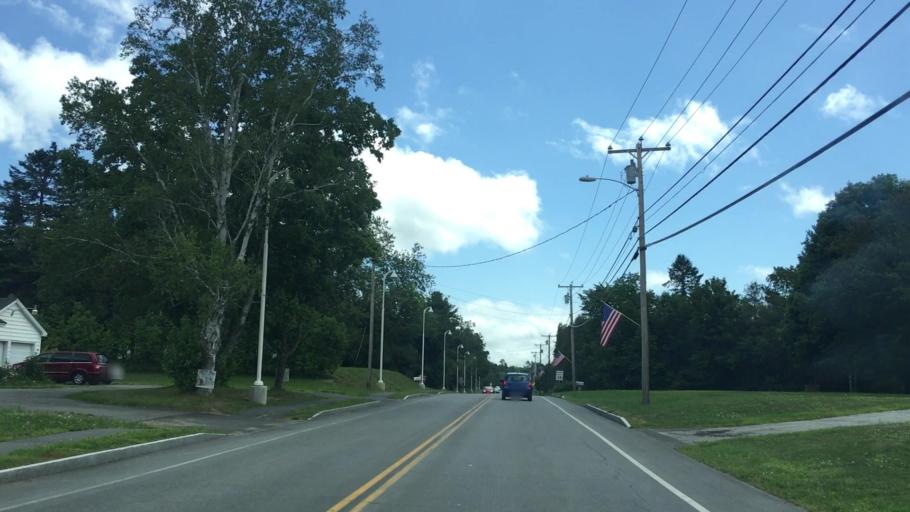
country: US
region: Maine
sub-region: Penobscot County
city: Hermon
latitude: 44.8080
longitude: -68.9069
